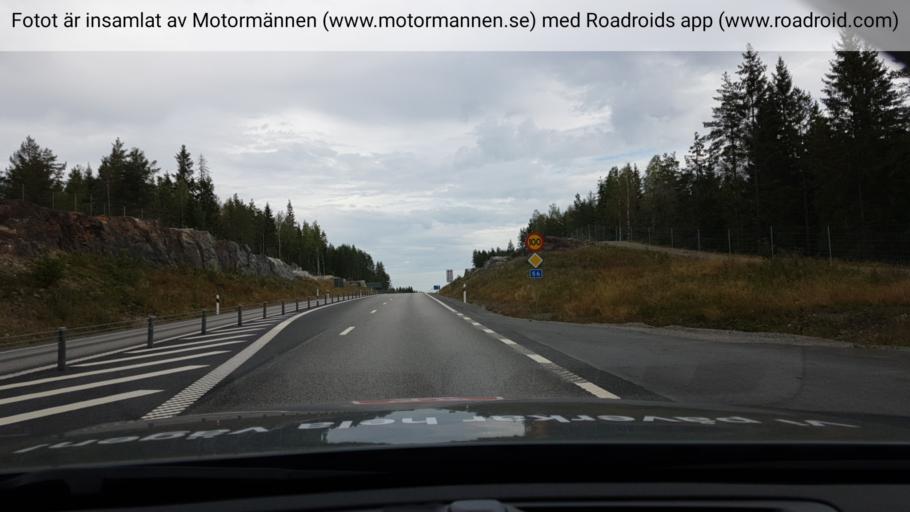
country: SE
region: Uppsala
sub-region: Heby Kommun
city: Heby
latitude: 60.0166
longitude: 16.8567
